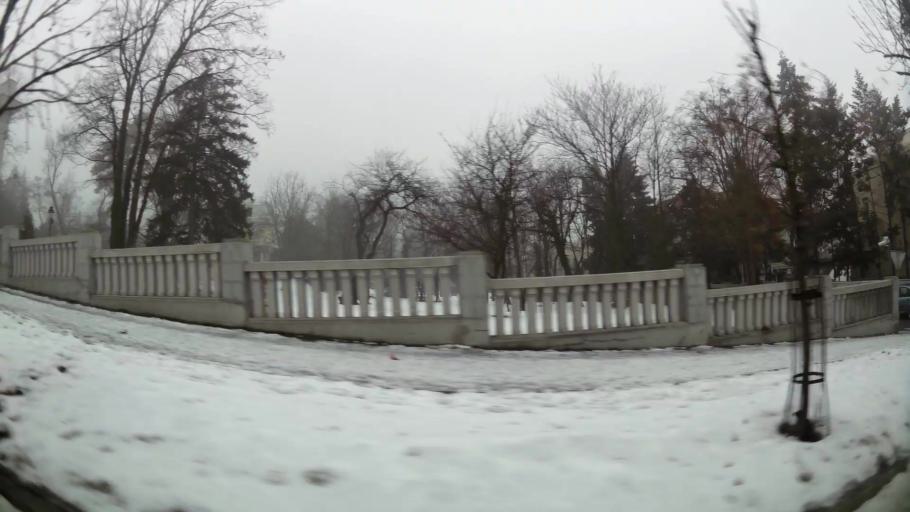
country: RS
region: Central Serbia
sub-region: Belgrade
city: Savski Venac
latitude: 44.7904
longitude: 20.4406
